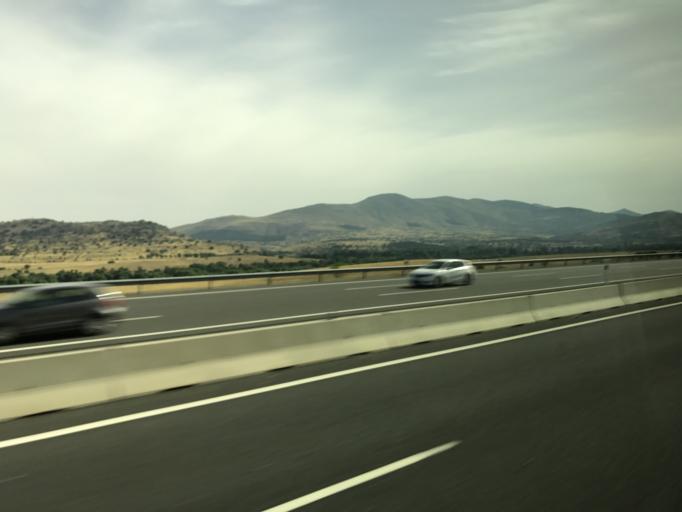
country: ES
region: Castille and Leon
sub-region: Provincia de Segovia
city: Vegas de Matute
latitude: 40.7388
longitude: -4.2275
